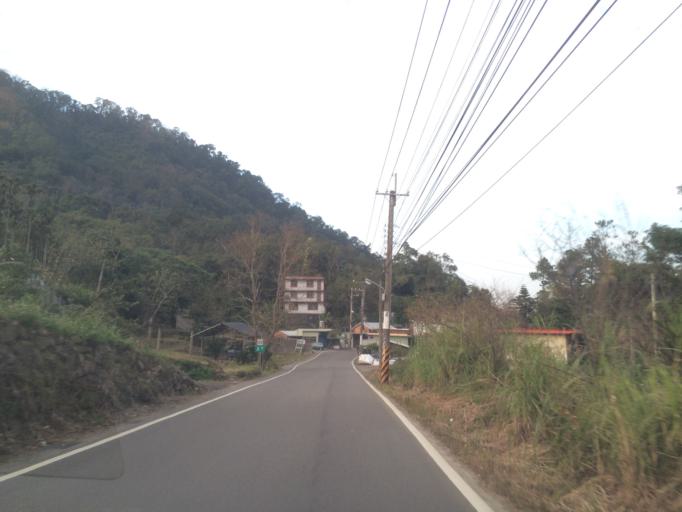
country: TW
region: Taiwan
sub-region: Hsinchu
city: Hsinchu
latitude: 24.6847
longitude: 121.1016
